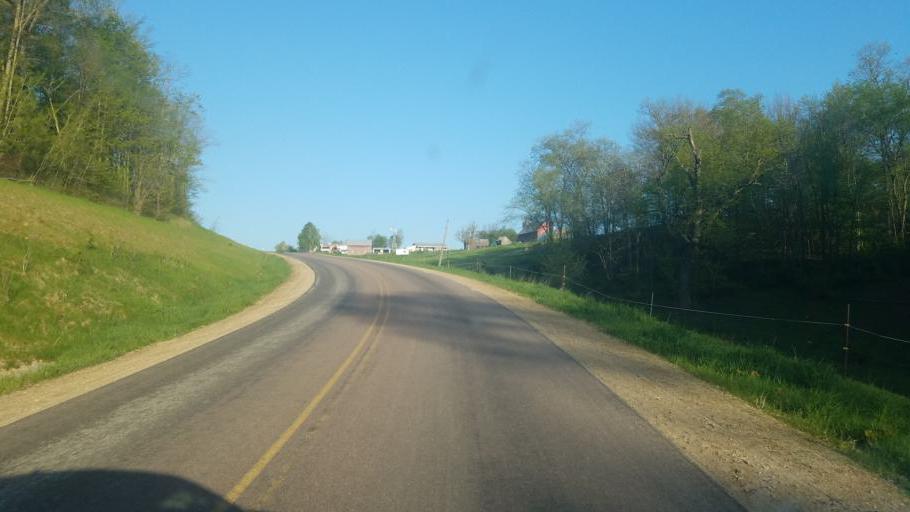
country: US
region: Wisconsin
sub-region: Vernon County
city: Hillsboro
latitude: 43.6464
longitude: -90.4411
